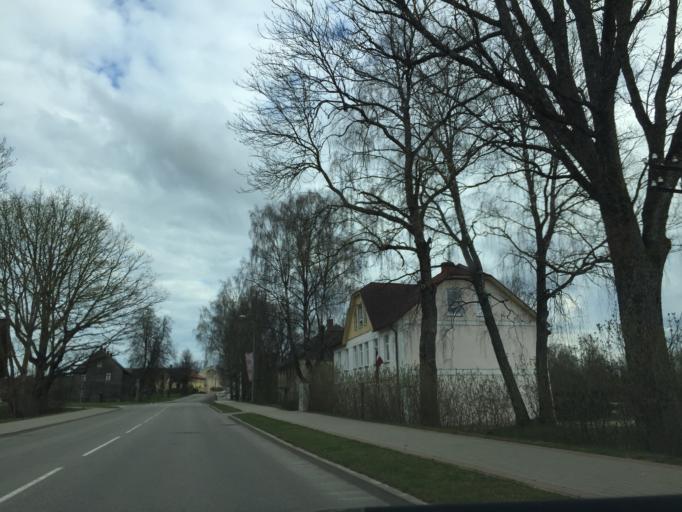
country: LV
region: Aluksnes Rajons
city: Aluksne
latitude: 57.4181
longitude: 27.0437
